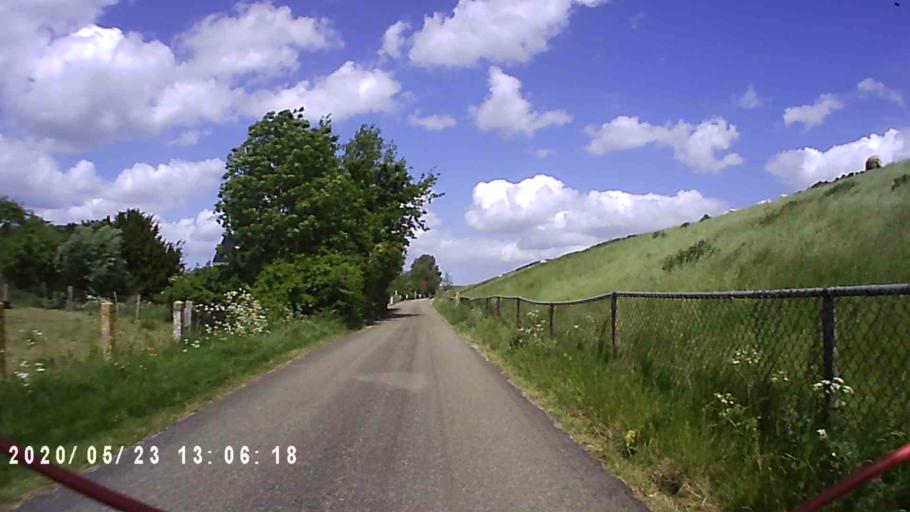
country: DE
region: Lower Saxony
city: Emden
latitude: 53.2964
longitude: 7.0756
